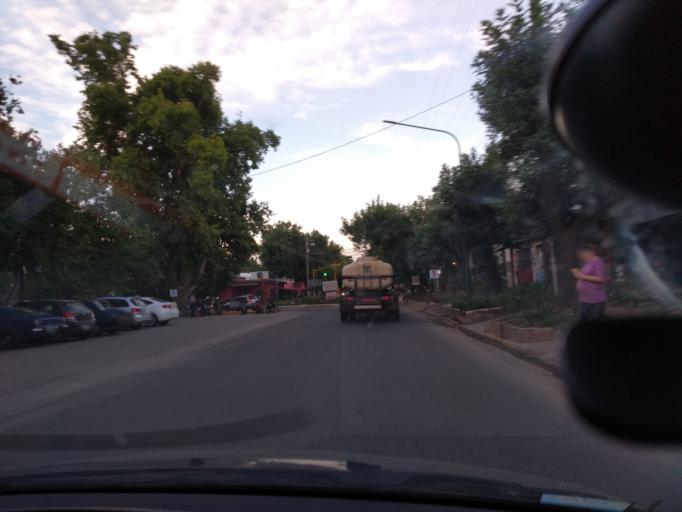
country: AR
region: Cordoba
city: Villa Las Rosas
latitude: -31.9473
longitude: -65.0515
